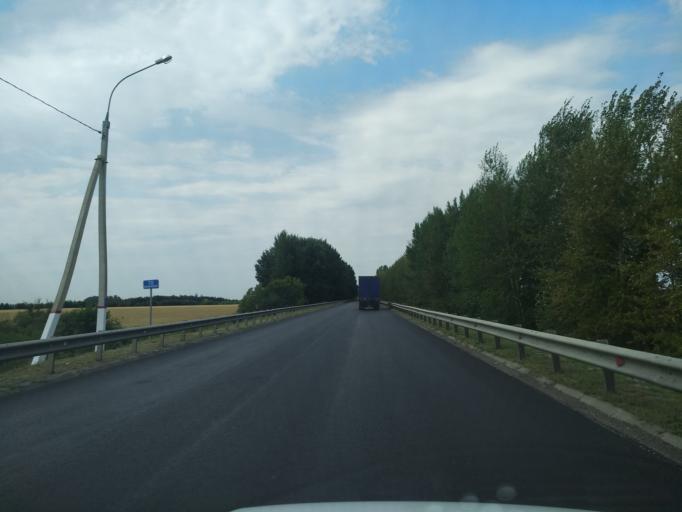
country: RU
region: Voronezj
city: Pereleshino
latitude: 51.7584
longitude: 40.1203
